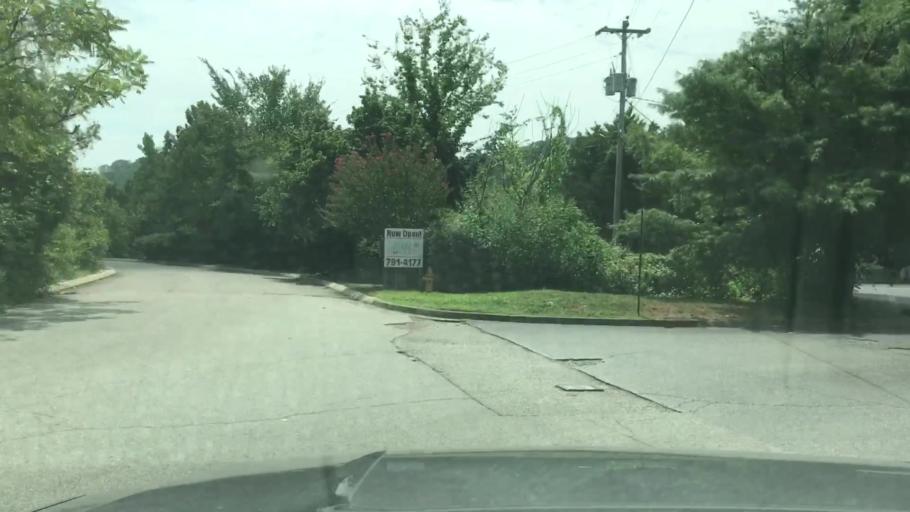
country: US
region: Tennessee
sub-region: Williamson County
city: Franklin
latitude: 35.9965
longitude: -86.8851
